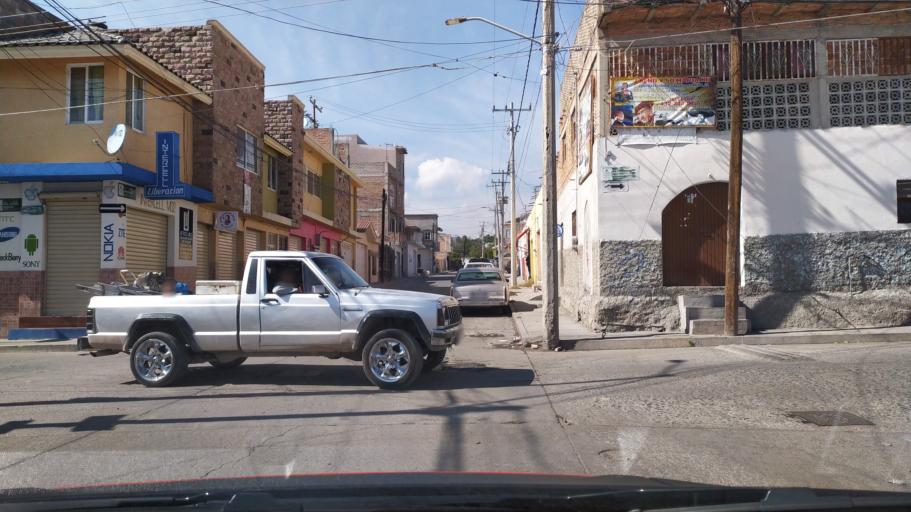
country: MX
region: Guanajuato
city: Ciudad Manuel Doblado
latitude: 20.7319
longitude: -101.9537
